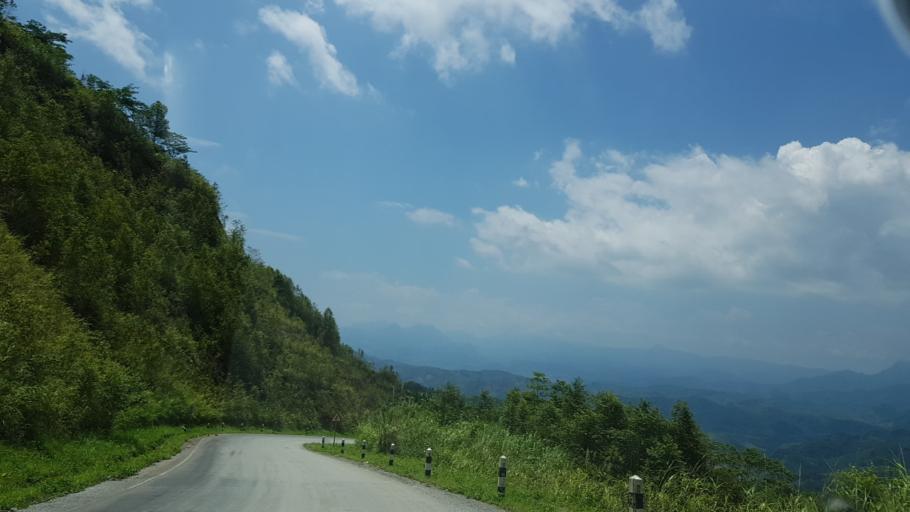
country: LA
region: Vientiane
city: Muang Kasi
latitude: 19.3829
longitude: 102.1532
